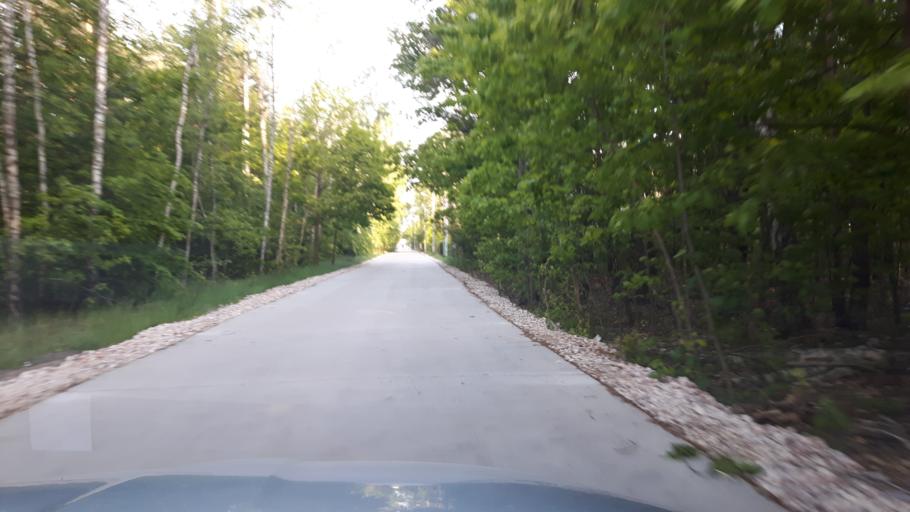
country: PL
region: Masovian Voivodeship
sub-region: Warszawa
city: Rembertow
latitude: 52.2778
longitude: 21.1530
